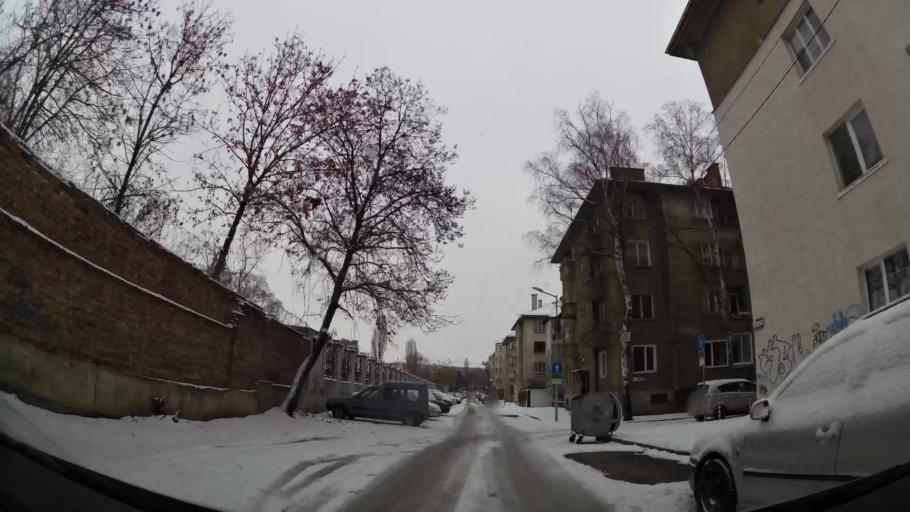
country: BG
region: Sofia-Capital
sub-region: Stolichna Obshtina
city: Sofia
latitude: 42.6880
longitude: 23.3492
